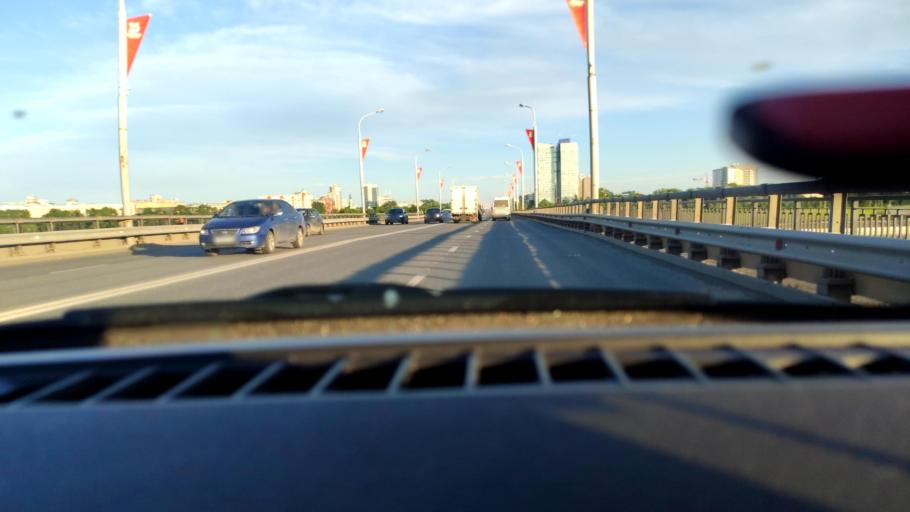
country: RU
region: Perm
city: Perm
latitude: 58.0231
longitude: 56.2235
